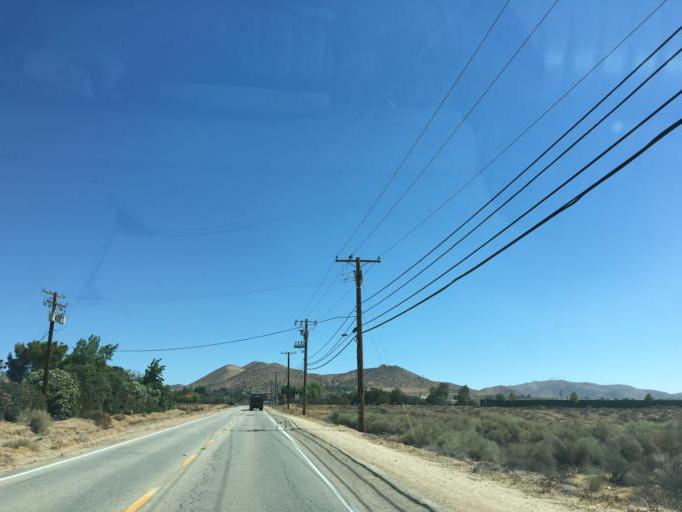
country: US
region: California
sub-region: Los Angeles County
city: Acton
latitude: 34.4776
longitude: -118.1692
